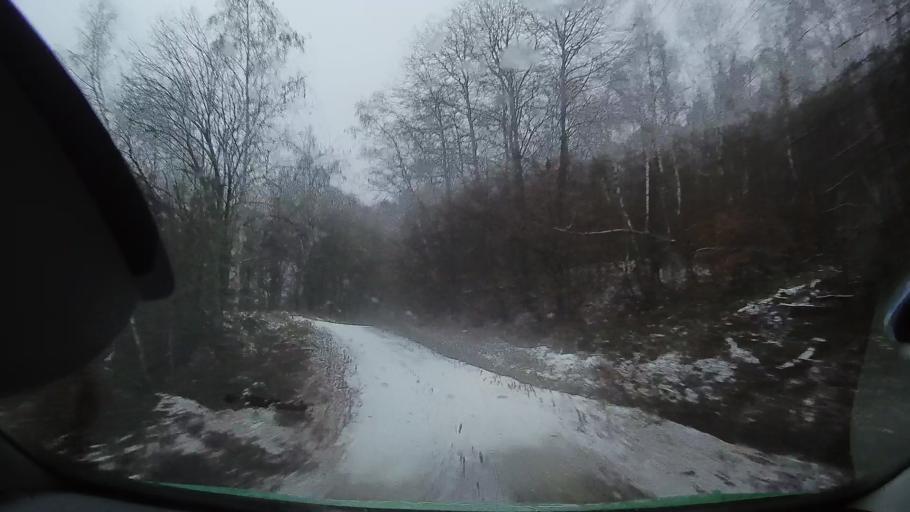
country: RO
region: Alba
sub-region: Comuna Avram Iancu
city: Avram Iancu
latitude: 46.3049
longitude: 22.7967
